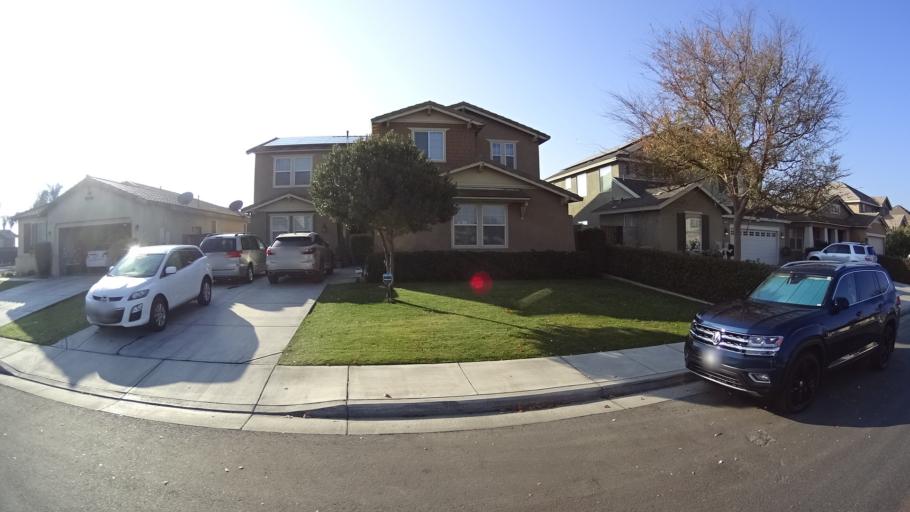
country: US
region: California
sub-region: Kern County
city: Greenacres
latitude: 35.3002
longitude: -119.1167
